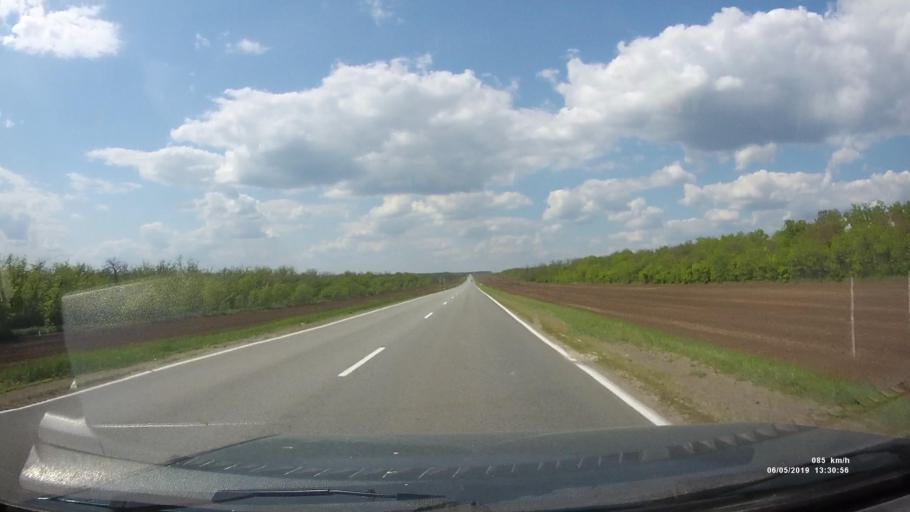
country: RU
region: Rostov
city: Ust'-Donetskiy
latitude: 47.6730
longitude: 40.8182
